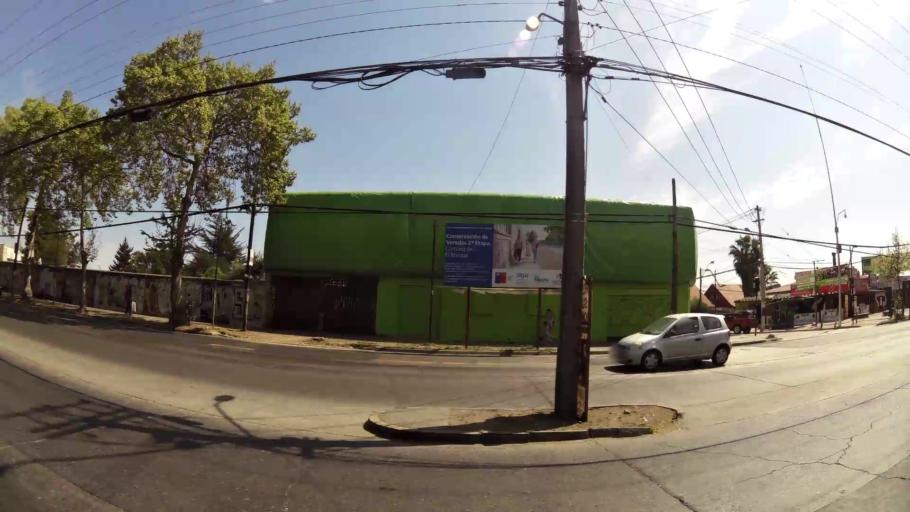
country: CL
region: Santiago Metropolitan
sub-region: Provincia de Santiago
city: La Pintana
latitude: -33.5493
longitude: -70.6712
